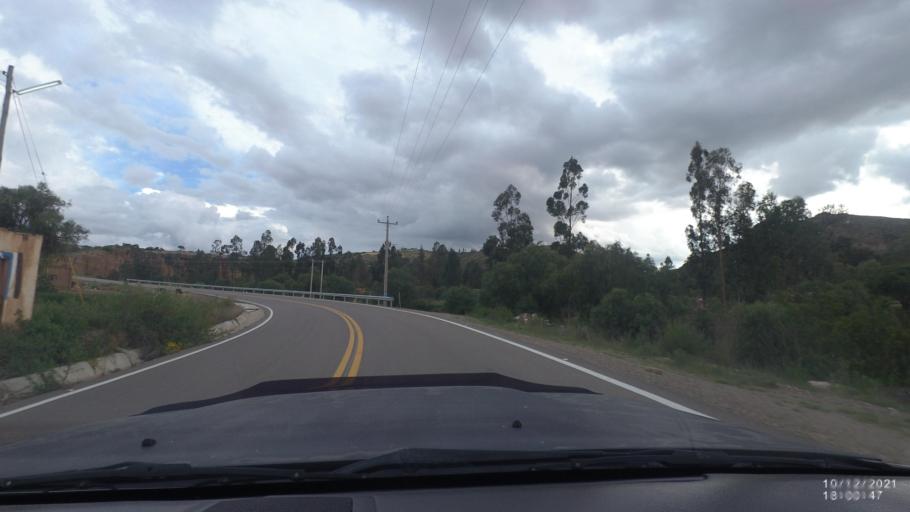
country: BO
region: Cochabamba
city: Cliza
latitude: -17.7452
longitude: -65.9218
